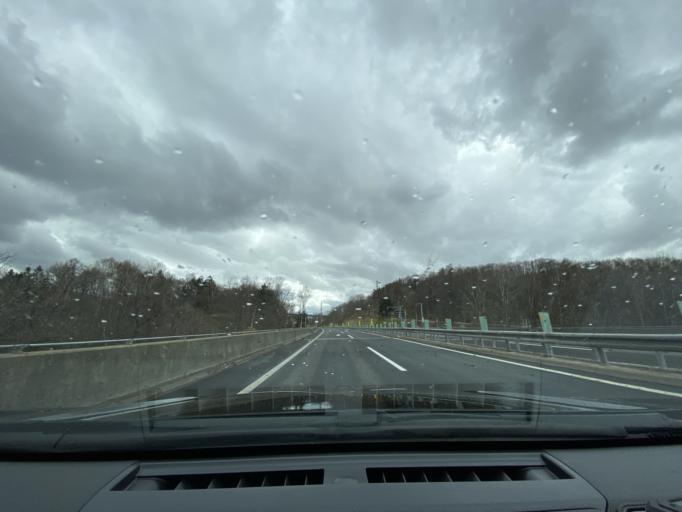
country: JP
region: Hokkaido
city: Takikawa
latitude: 43.5430
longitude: 141.9360
